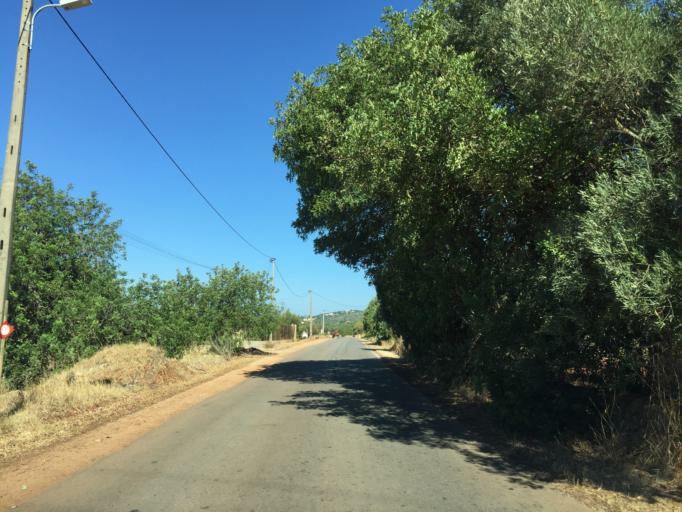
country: PT
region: Faro
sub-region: Loule
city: Almancil
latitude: 37.1071
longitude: -8.0636
